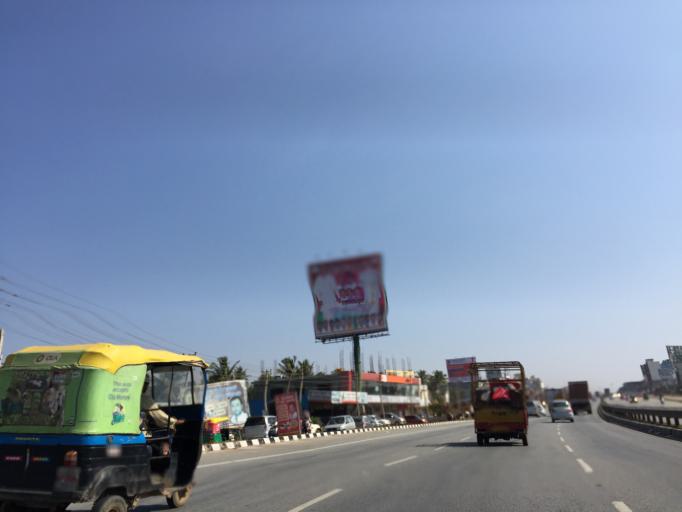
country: IN
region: Karnataka
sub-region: Bangalore Rural
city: Hoskote
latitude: 13.0668
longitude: 77.7773
